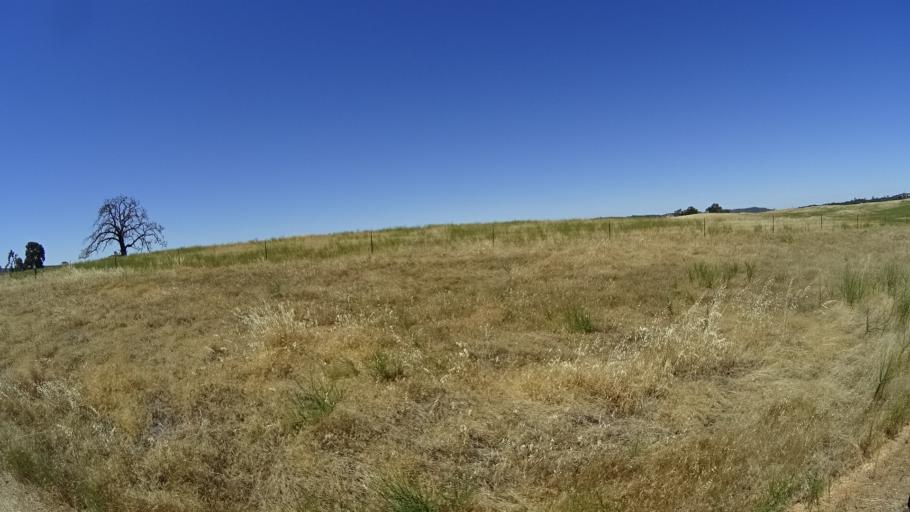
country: US
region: California
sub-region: Calaveras County
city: Copperopolis
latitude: 38.0493
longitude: -120.7331
